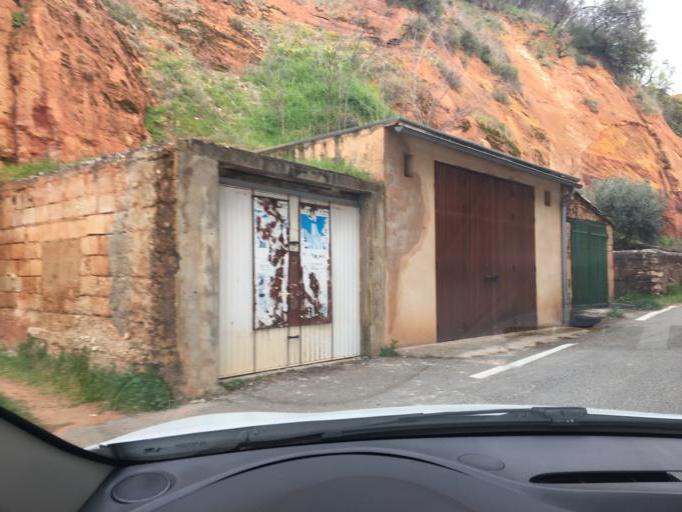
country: FR
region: Provence-Alpes-Cote d'Azur
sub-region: Departement du Vaucluse
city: Roussillon
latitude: 43.9026
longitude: 5.2899
